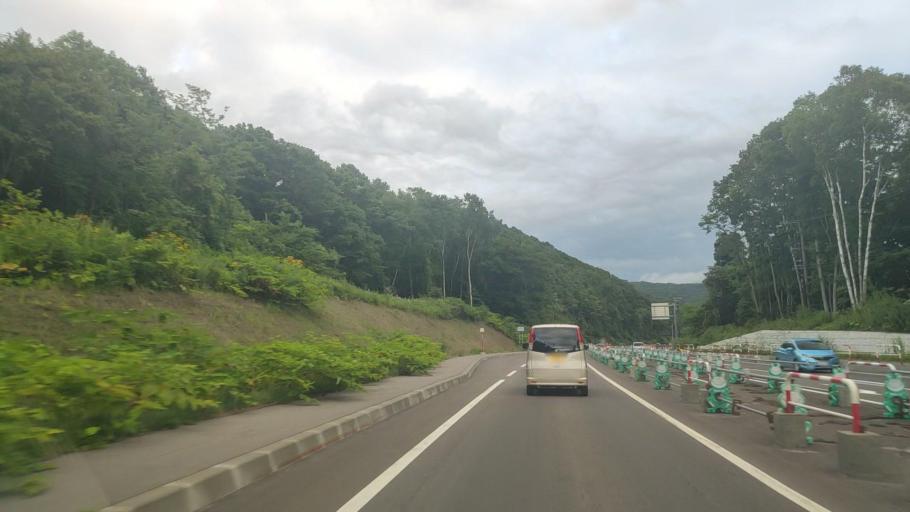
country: JP
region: Hokkaido
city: Nanae
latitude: 41.9885
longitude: 140.6391
